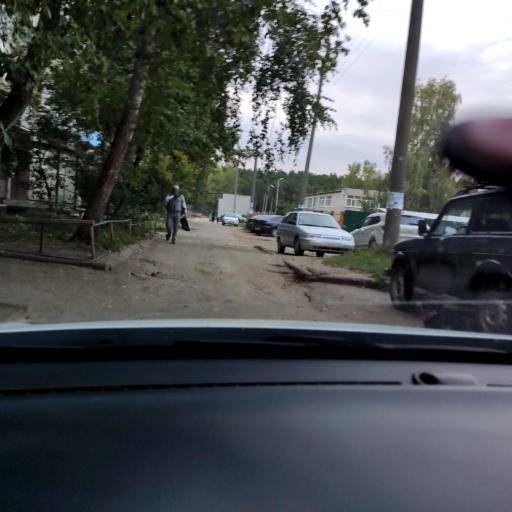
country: RU
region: Mariy-El
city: Volzhsk
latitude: 55.8663
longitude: 48.3456
